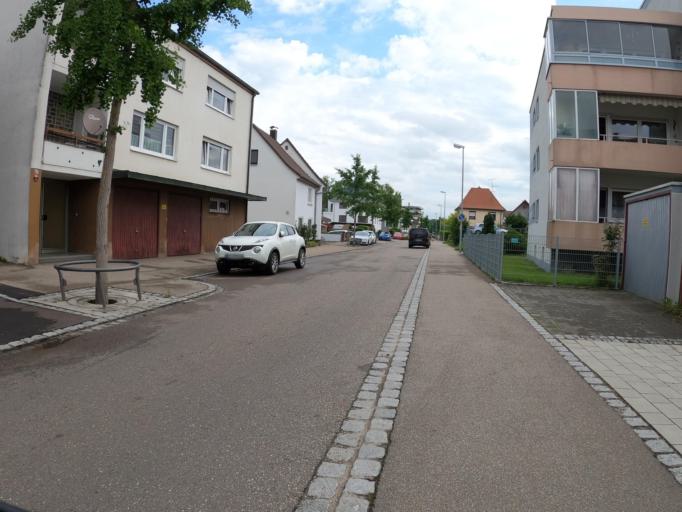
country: DE
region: Baden-Wuerttemberg
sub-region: Tuebingen Region
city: Langenau
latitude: 48.4985
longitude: 10.1255
